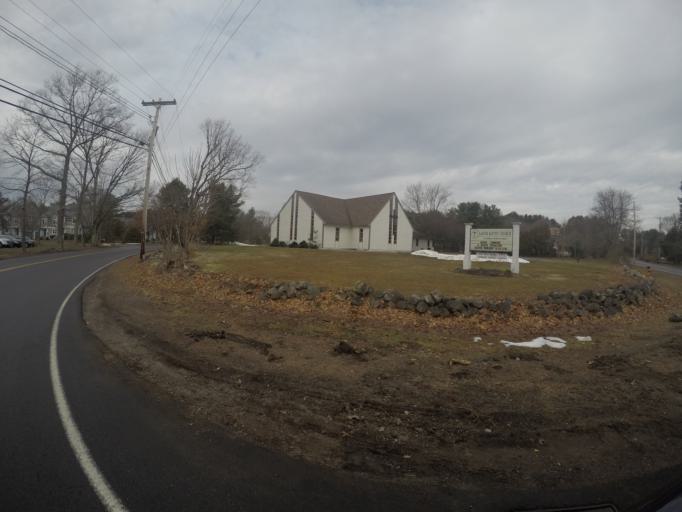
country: US
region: Massachusetts
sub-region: Bristol County
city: Easton
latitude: 42.0507
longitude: -71.1295
